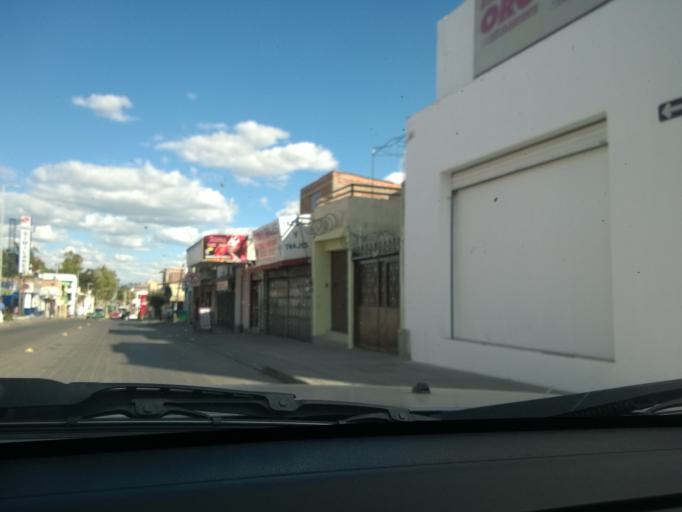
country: MX
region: Guanajuato
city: Leon
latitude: 21.1325
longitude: -101.6930
